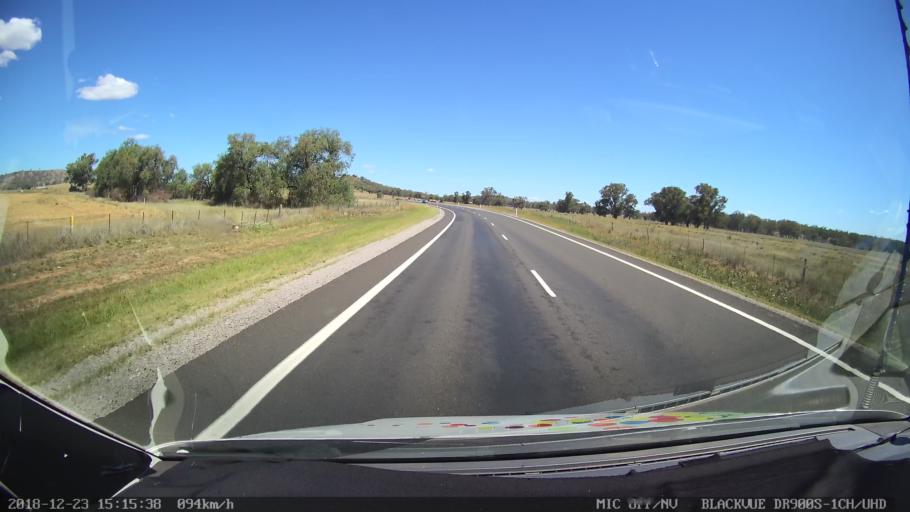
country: AU
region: New South Wales
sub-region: Tamworth Municipality
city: Manilla
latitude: -30.7886
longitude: 150.7437
